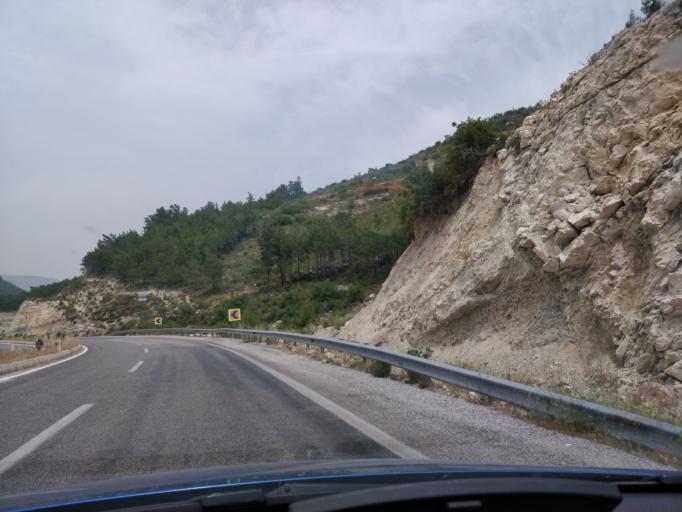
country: TR
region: Mersin
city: Tasucu
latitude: 36.3939
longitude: 33.8424
